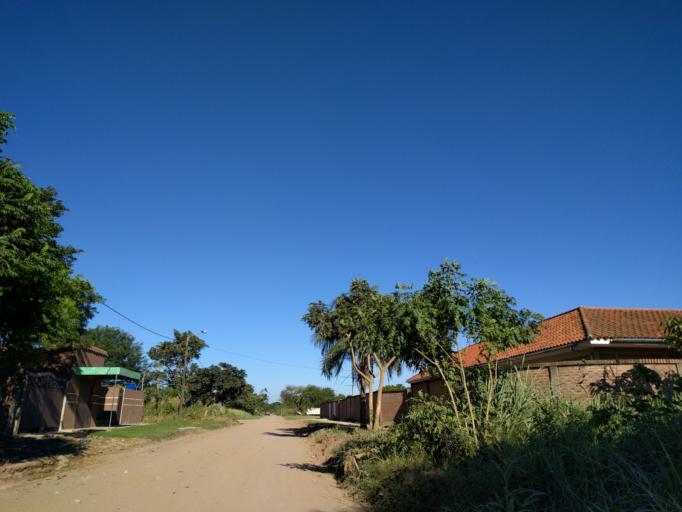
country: BO
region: Santa Cruz
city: Santa Cruz de la Sierra
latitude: -17.8474
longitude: -63.2369
